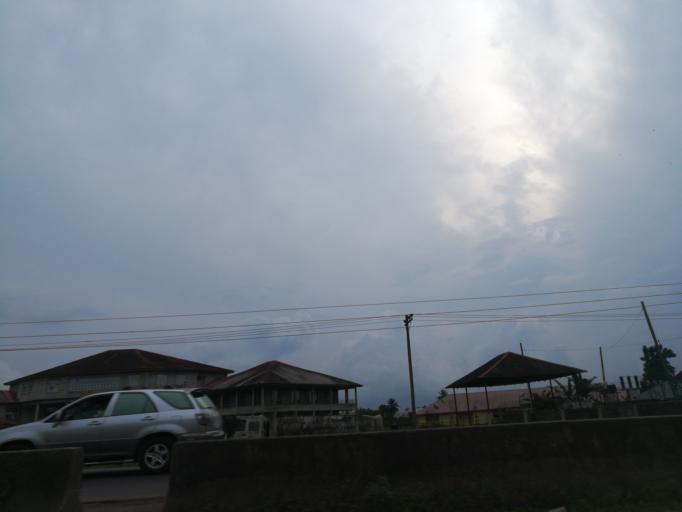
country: NG
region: Rivers
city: Okrika
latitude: 4.7786
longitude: 7.1274
